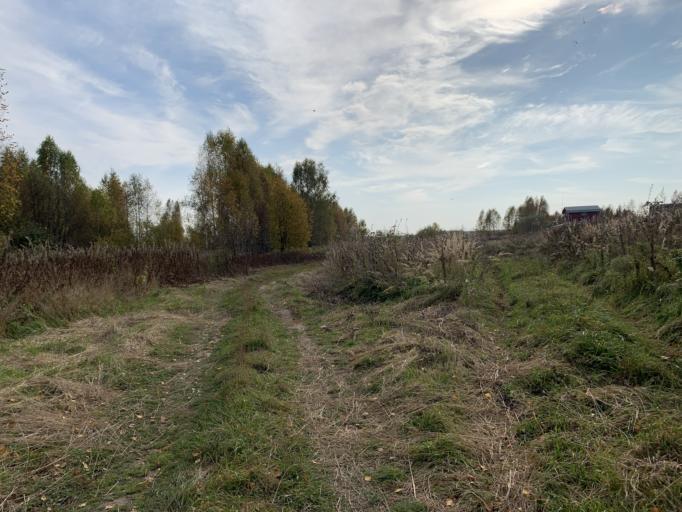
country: RU
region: Jaroslavl
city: Porech'ye-Rybnoye
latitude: 56.9801
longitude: 39.3868
